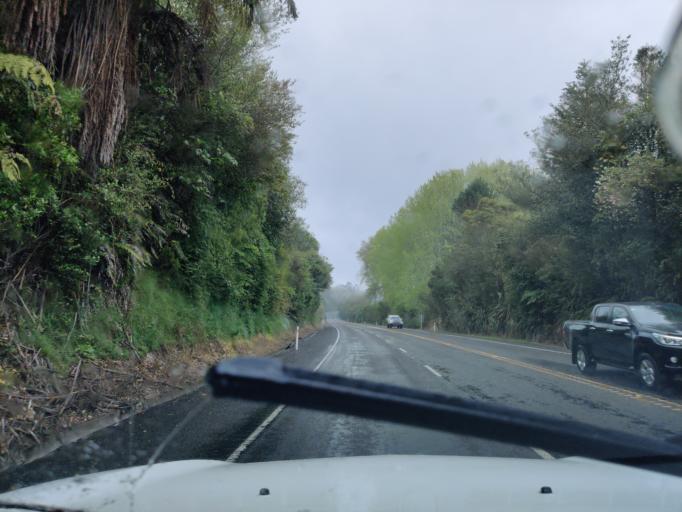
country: NZ
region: Bay of Plenty
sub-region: Rotorua District
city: Rotorua
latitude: -38.0728
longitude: 176.1696
